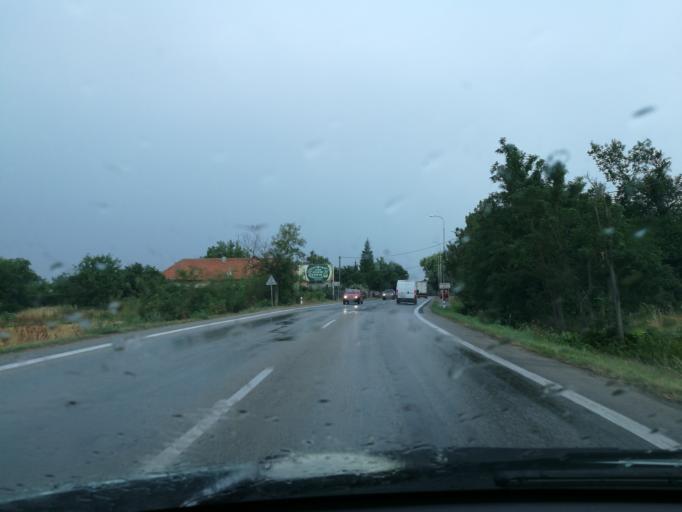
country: SK
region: Nitriansky
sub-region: Okres Komarno
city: Hurbanovo
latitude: 47.8553
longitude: 18.1732
